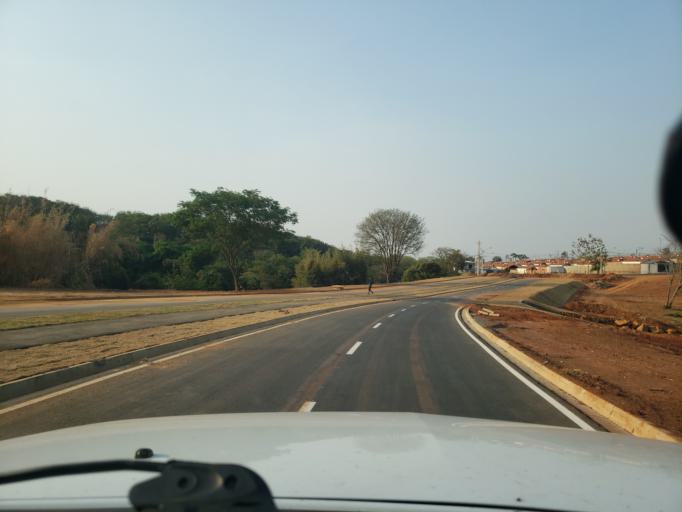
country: BR
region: Sao Paulo
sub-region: Moji-Guacu
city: Mogi-Gaucu
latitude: -22.3167
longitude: -46.9463
